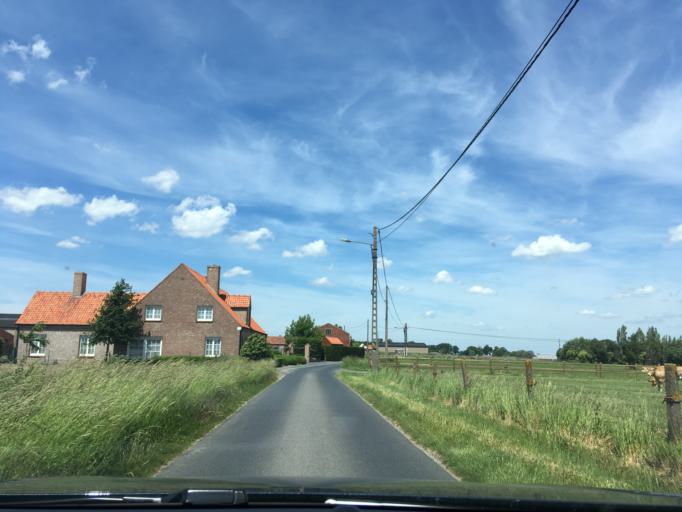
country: BE
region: Flanders
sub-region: Provincie West-Vlaanderen
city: Ardooie
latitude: 51.0139
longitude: 3.1936
